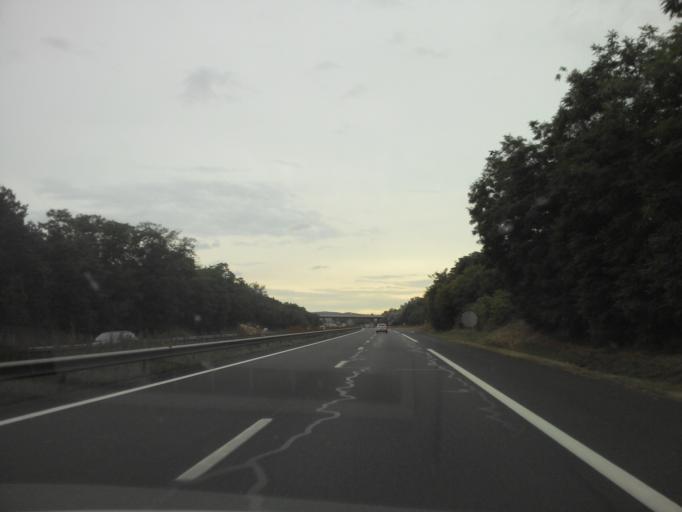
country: FR
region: Auvergne
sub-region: Departement du Puy-de-Dome
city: Saint-Bonnet-pres-Riom
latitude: 45.9228
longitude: 3.1450
